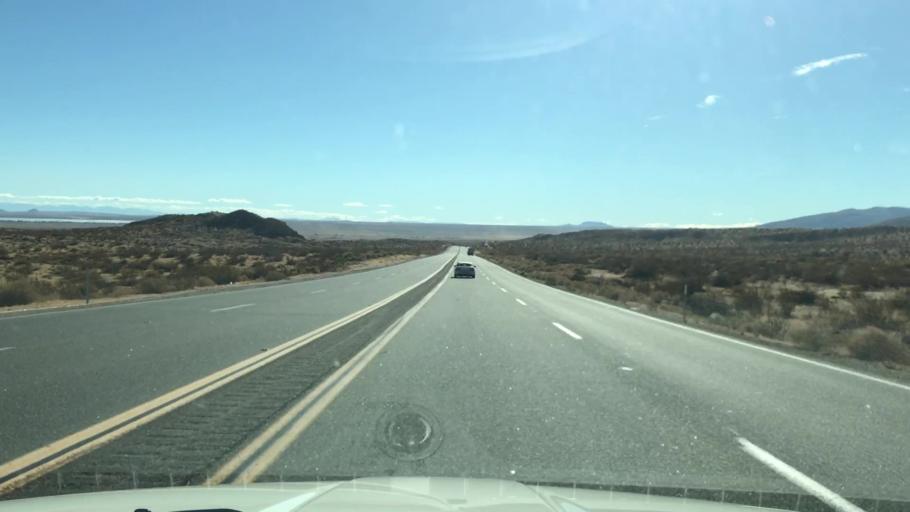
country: US
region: California
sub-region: Kern County
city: California City
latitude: 35.3292
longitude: -117.9749
